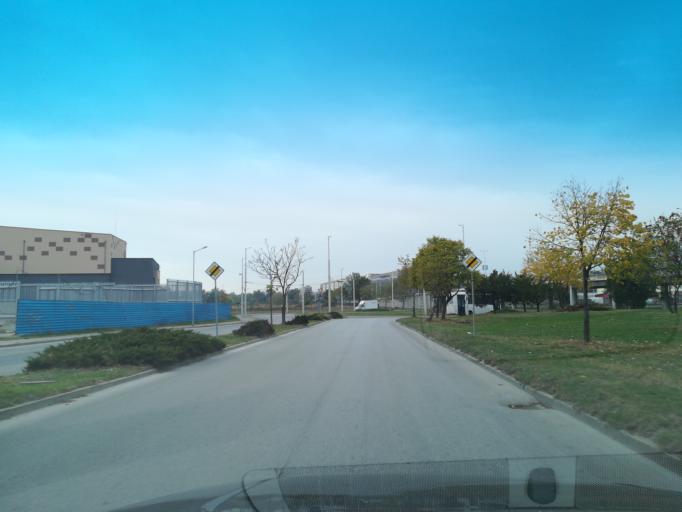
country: BG
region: Plovdiv
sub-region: Obshtina Plovdiv
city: Plovdiv
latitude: 42.1471
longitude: 24.7983
